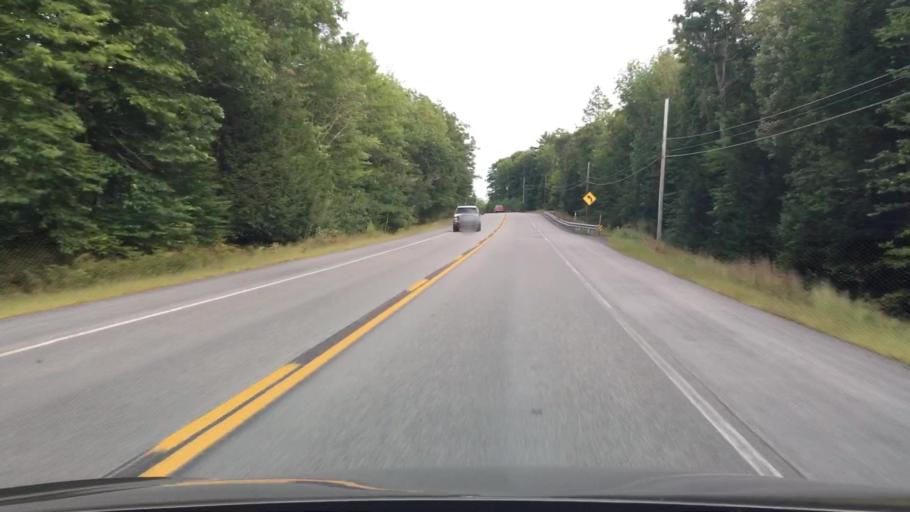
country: US
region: Maine
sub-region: Cumberland County
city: Bridgton
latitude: 44.0669
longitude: -70.7608
